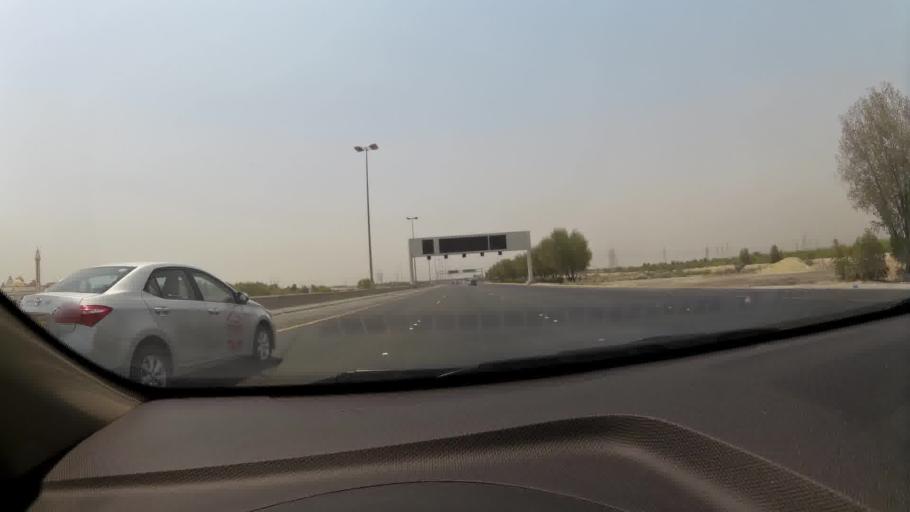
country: KW
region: Al Asimah
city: Ar Rabiyah
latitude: 29.3117
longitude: 47.7956
